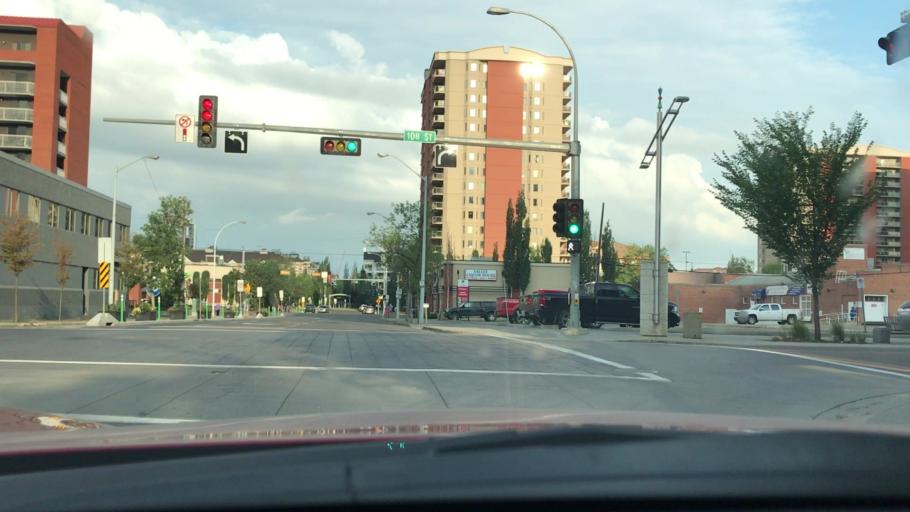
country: CA
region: Alberta
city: Edmonton
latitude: 53.5430
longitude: -113.5064
